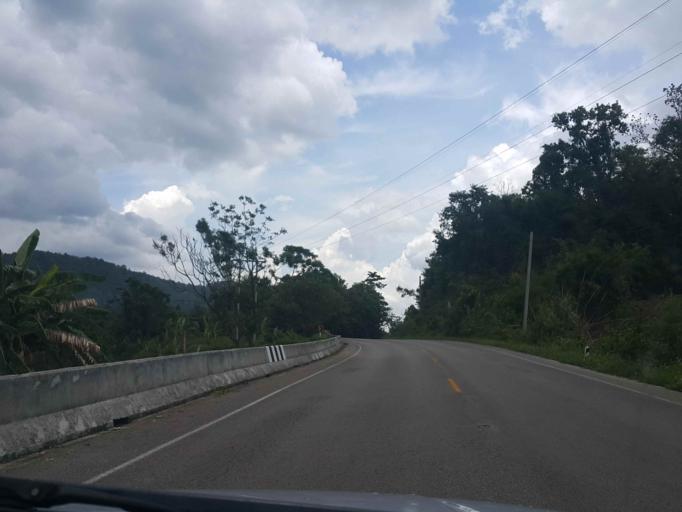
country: TH
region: Lampang
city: Ngao
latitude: 18.9280
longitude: 100.0949
